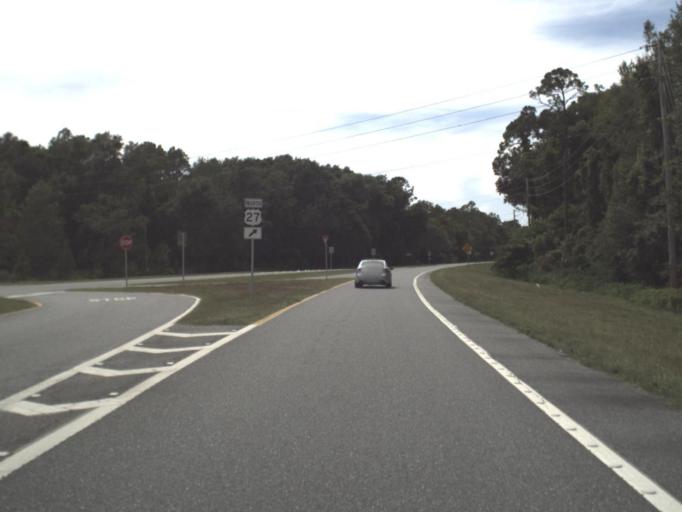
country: US
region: Florida
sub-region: Taylor County
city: Perry
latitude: 30.0816
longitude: -83.5199
